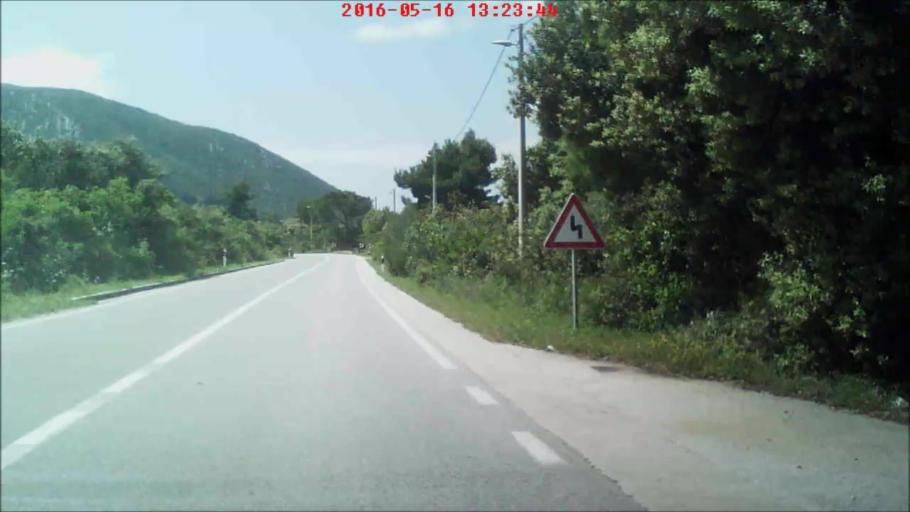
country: HR
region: Dubrovacko-Neretvanska
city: Ston
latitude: 42.8439
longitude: 17.7100
